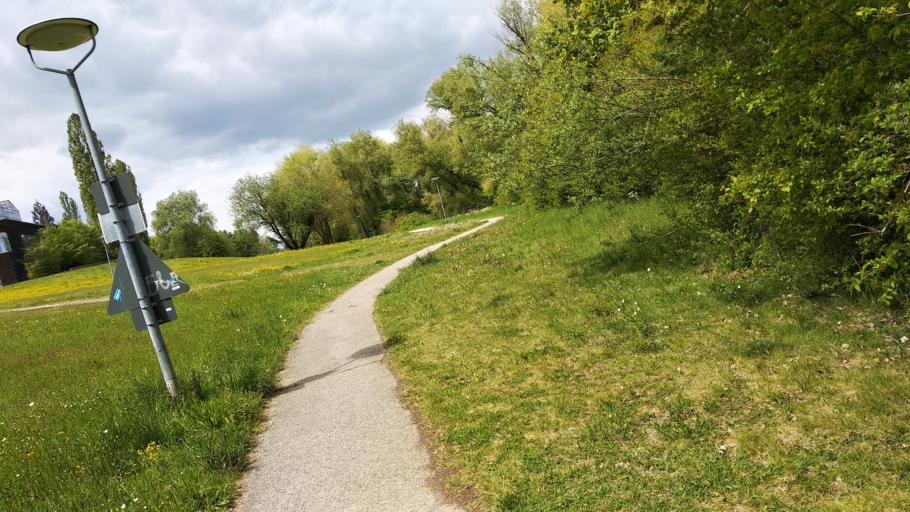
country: DE
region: Bavaria
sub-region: Upper Bavaria
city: Freising
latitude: 48.4006
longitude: 11.7225
